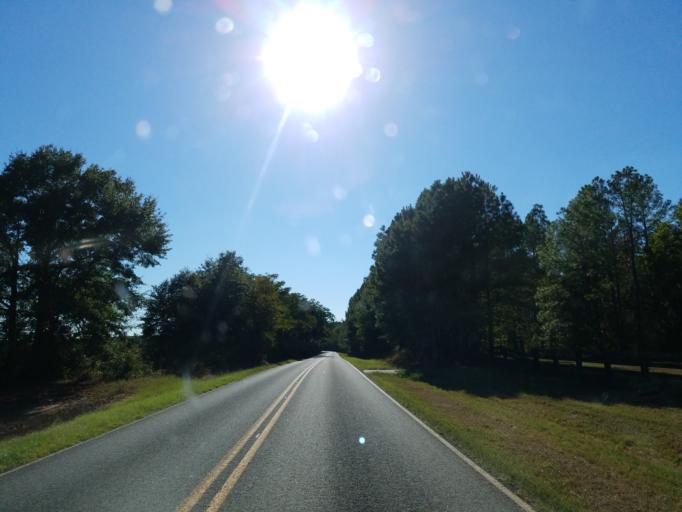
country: US
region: Georgia
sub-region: Dooly County
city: Unadilla
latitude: 32.2383
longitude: -83.8668
